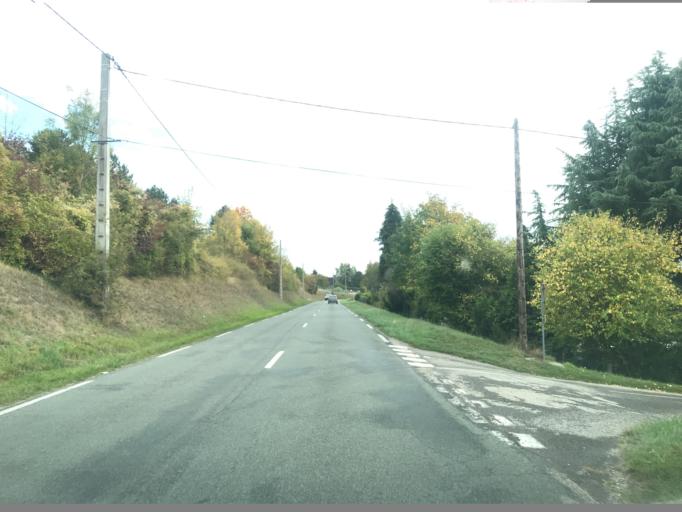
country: FR
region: Haute-Normandie
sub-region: Departement de l'Eure
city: Heudreville-sur-Eure
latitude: 49.1354
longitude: 1.2077
